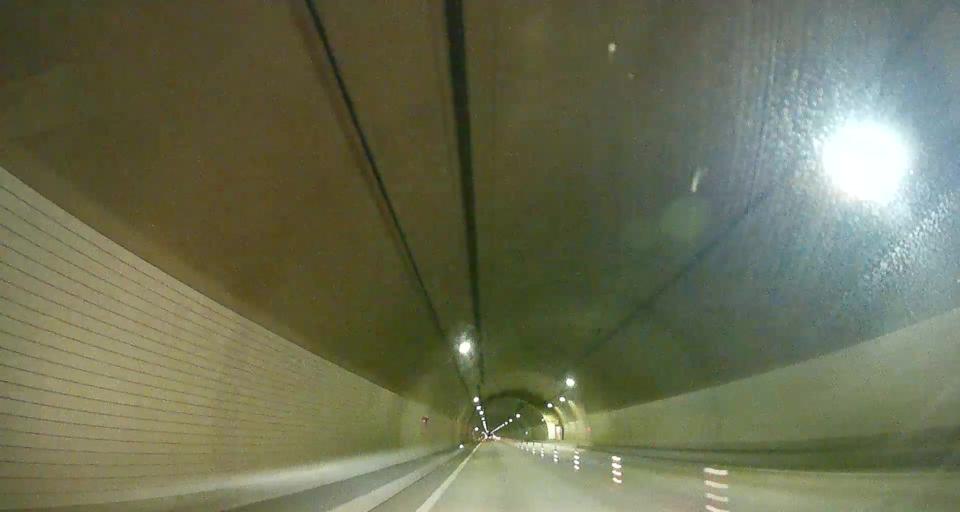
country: JP
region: Iwate
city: Miyako
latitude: 39.9290
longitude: 141.8710
